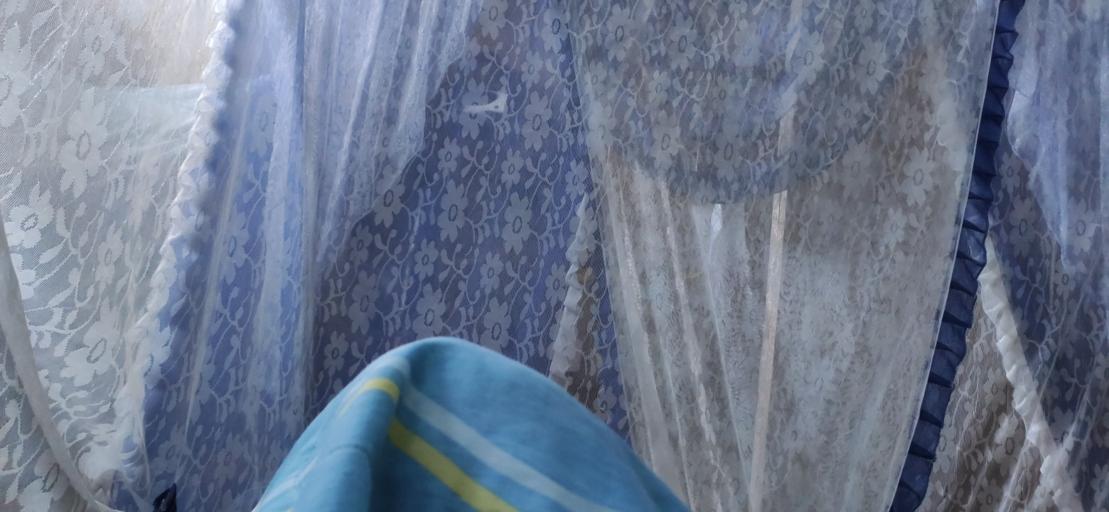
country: CO
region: Putumayo
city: Puerto Asis
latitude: 0.1140
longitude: -76.2945
